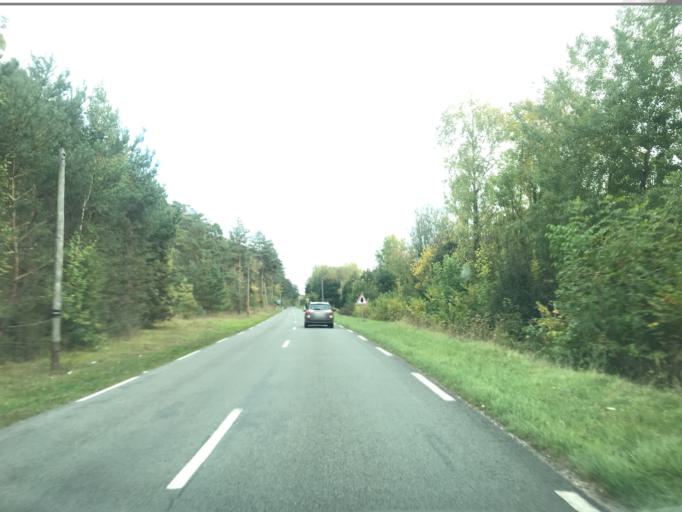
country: FR
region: Haute-Normandie
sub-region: Departement de l'Eure
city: Heudreville-sur-Eure
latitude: 49.1428
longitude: 1.1991
